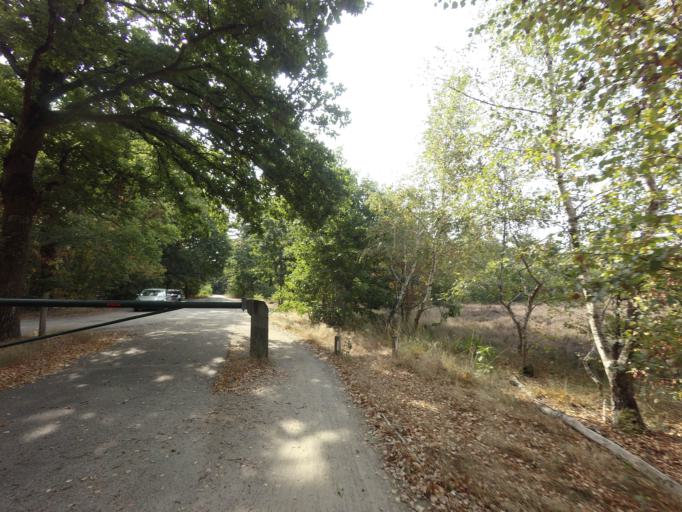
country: NL
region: North Brabant
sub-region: Gemeente Sint Anthonis
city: Sint Anthonis
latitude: 51.6015
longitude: 5.8278
